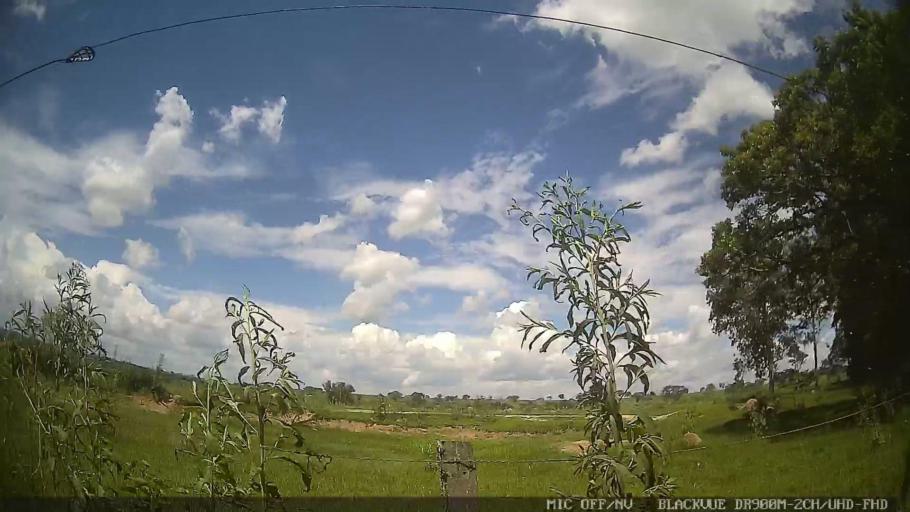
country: BR
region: Sao Paulo
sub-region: Conchas
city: Conchas
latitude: -23.0404
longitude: -47.9948
